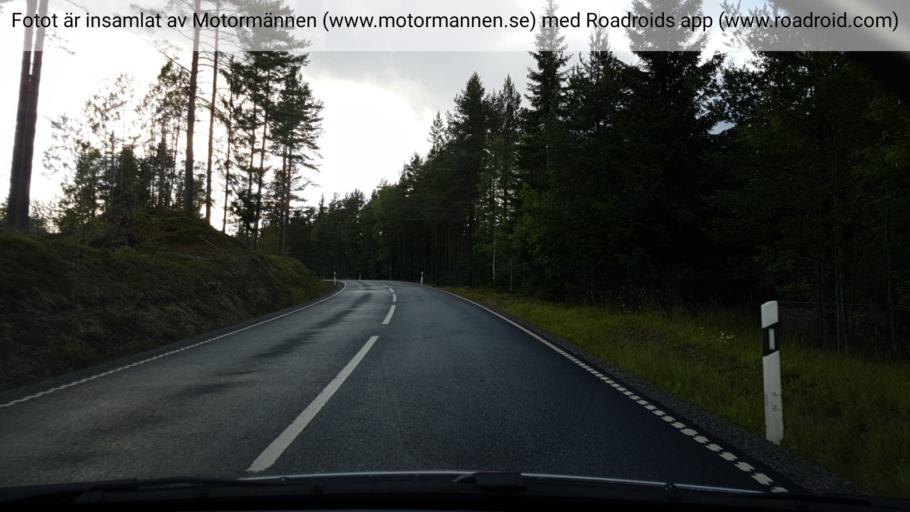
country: SE
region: OErebro
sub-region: Hallefors Kommun
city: Haellefors
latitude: 59.8194
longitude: 14.6465
